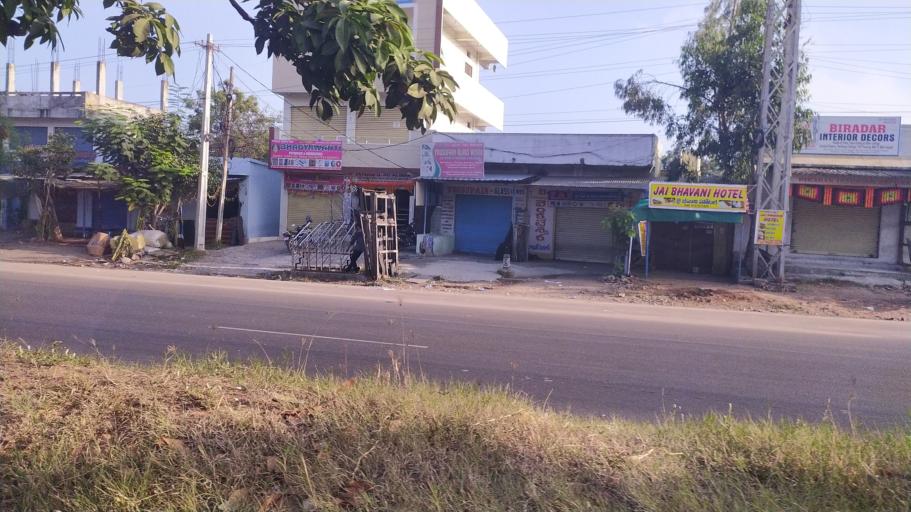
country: IN
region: Telangana
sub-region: Rangareddi
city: Balapur
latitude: 17.3194
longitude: 78.4351
